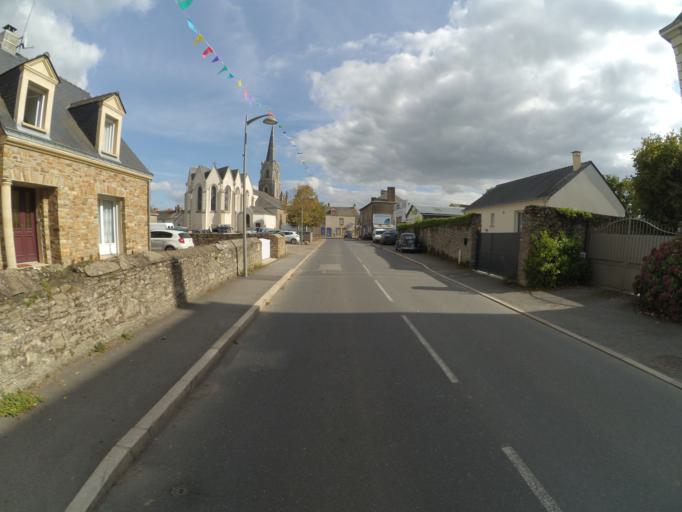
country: FR
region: Pays de la Loire
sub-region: Departement de la Loire-Atlantique
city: Casson
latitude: 47.3863
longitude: -1.5605
